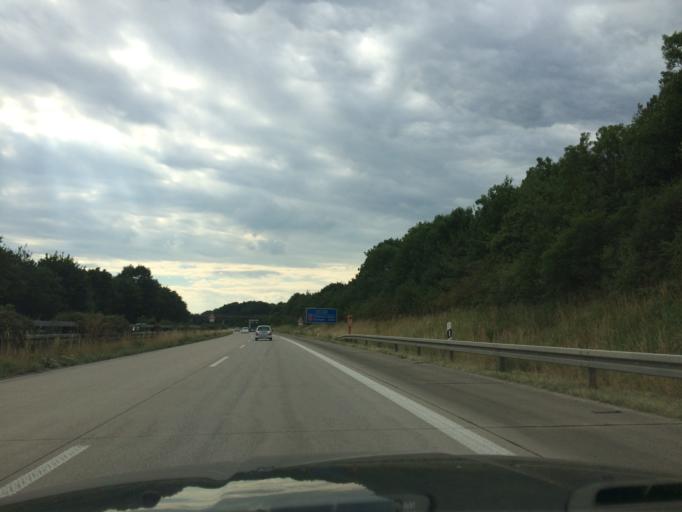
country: DE
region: North Rhine-Westphalia
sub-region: Regierungsbezirk Dusseldorf
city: Goch
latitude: 51.6735
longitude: 6.1116
